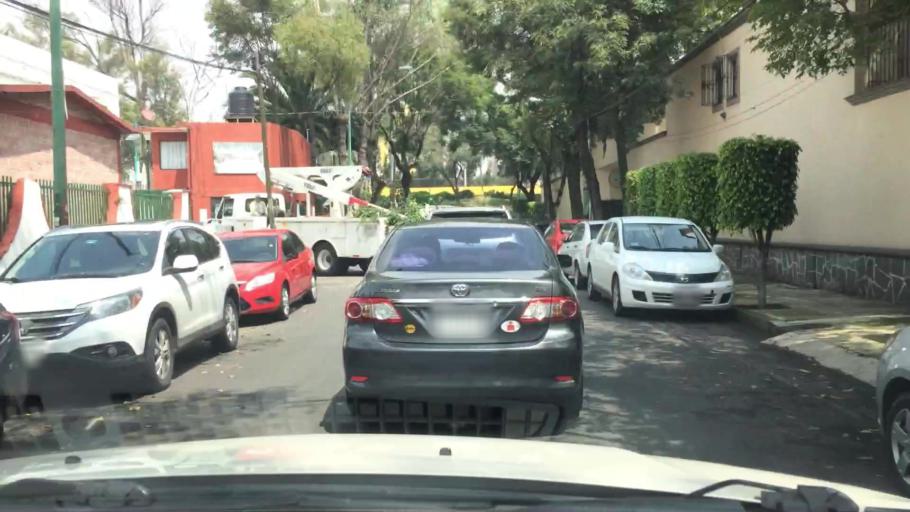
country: MX
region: Mexico City
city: Coyoacan
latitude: 19.3565
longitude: -99.1489
